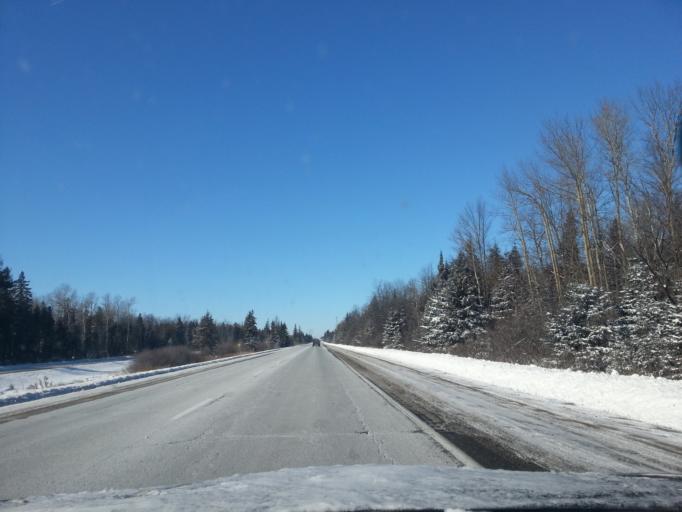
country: CA
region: Ontario
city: Carleton Place
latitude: 45.3169
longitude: -76.0764
